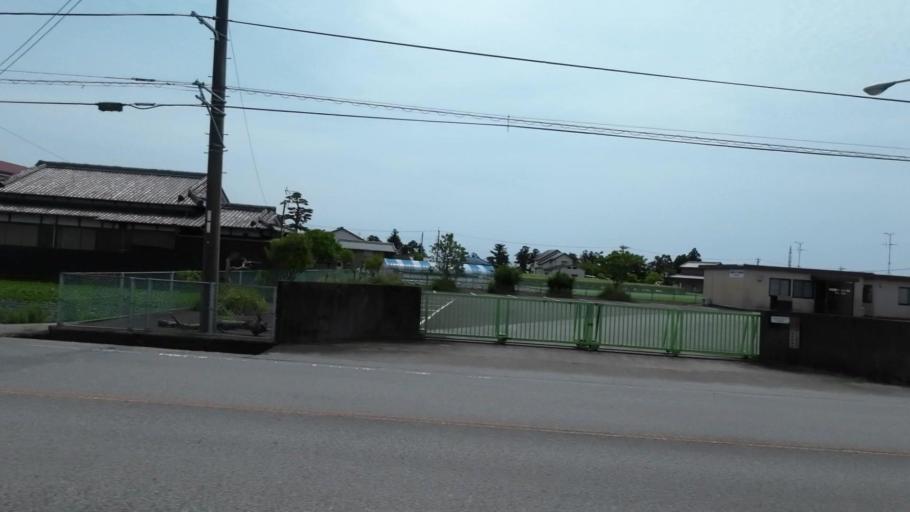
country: JP
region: Kochi
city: Kochi-shi
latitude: 33.5833
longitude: 133.6523
